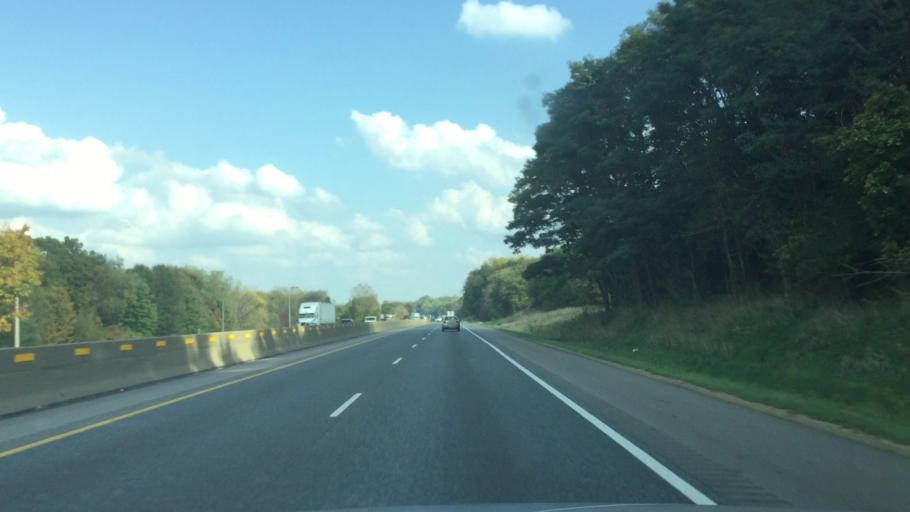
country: US
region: Michigan
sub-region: Kalamazoo County
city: Galesburg
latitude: 42.2702
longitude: -85.4716
